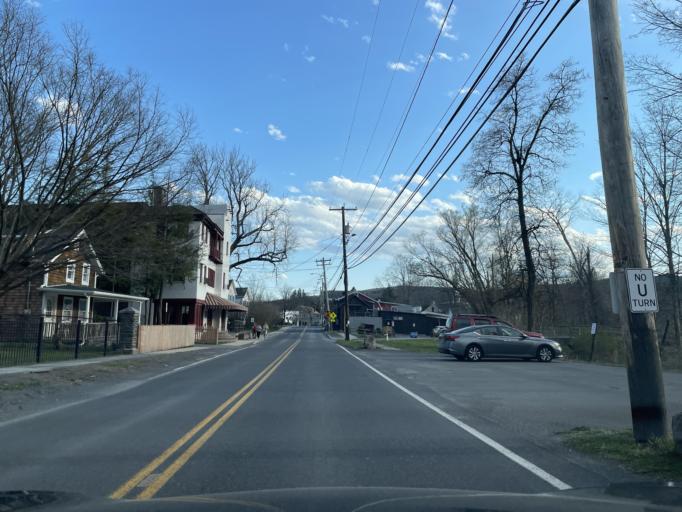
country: US
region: New York
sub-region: Ulster County
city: Woodstock
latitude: 42.0430
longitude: -74.1182
